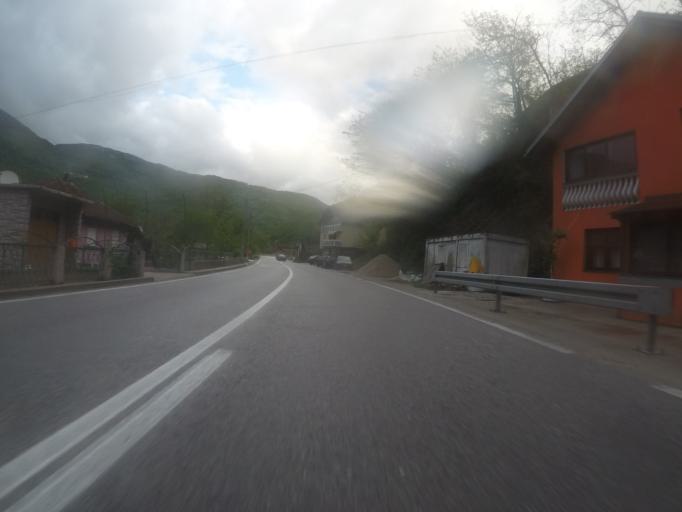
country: BA
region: Federation of Bosnia and Herzegovina
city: Jablanica
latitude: 43.6805
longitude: 17.7808
